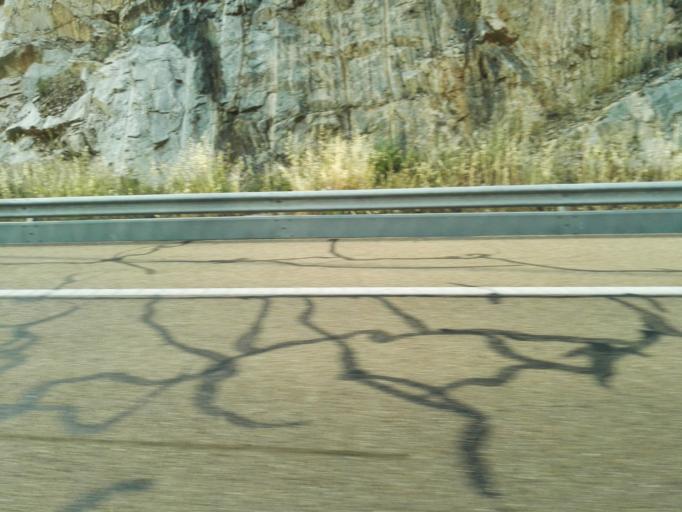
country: PT
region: Portalegre
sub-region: Elvas
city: Elvas
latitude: 38.9027
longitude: -7.1430
